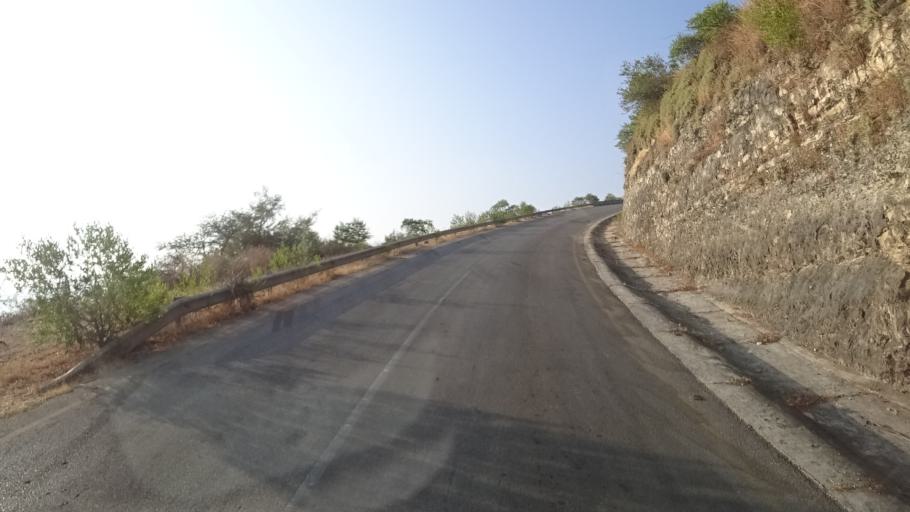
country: YE
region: Al Mahrah
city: Hawf
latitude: 16.7657
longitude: 53.3372
